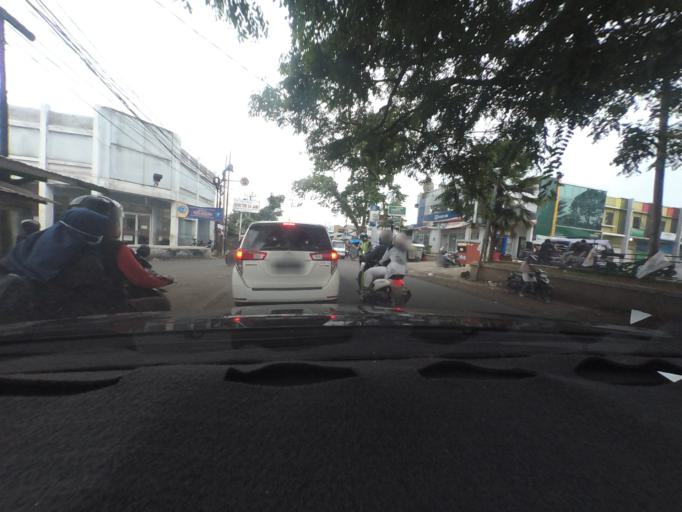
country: ID
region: West Java
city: Cicurug
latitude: -6.7971
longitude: 106.7774
